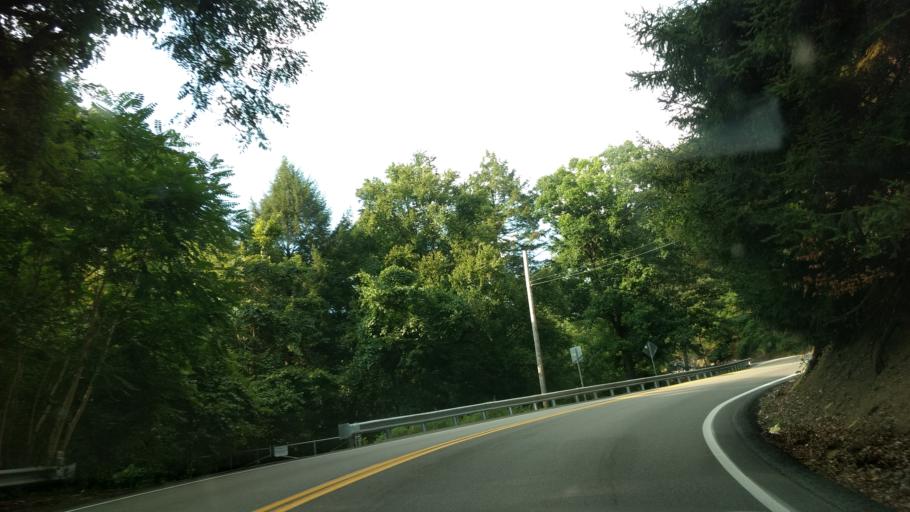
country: US
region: Pennsylvania
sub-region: Allegheny County
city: Glenshaw
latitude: 40.5338
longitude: -79.9787
